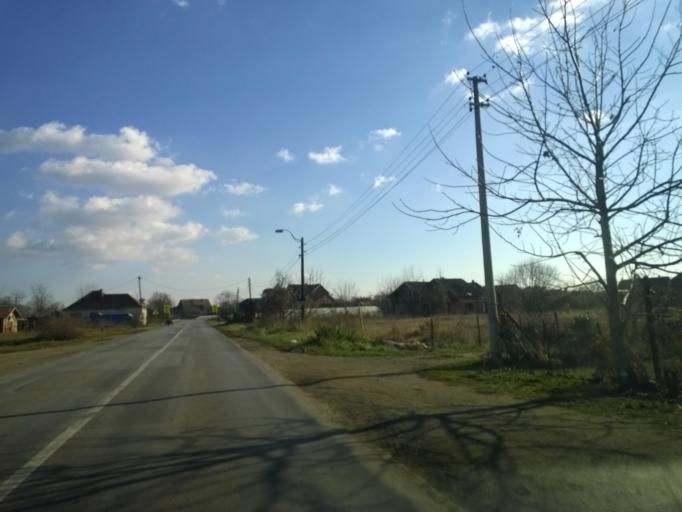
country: RS
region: Central Serbia
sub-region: Podunavski Okrug
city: Smederevo
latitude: 44.5963
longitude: 20.9683
